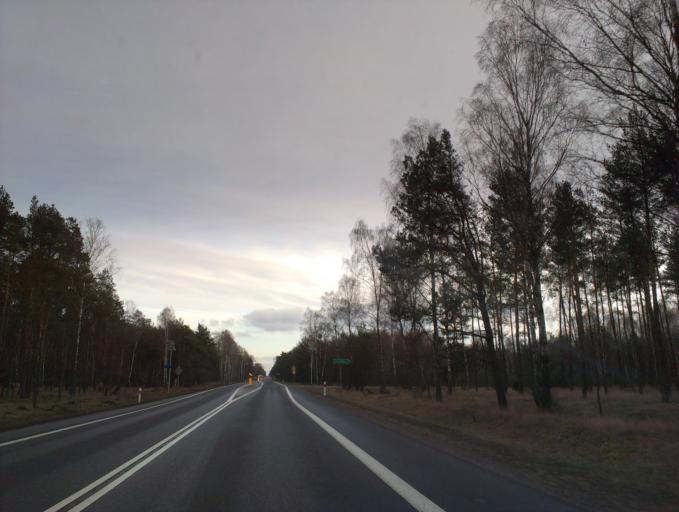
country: PL
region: Masovian Voivodeship
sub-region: Powiat sierpecki
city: Szczutowo
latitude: 52.8857
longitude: 19.5805
